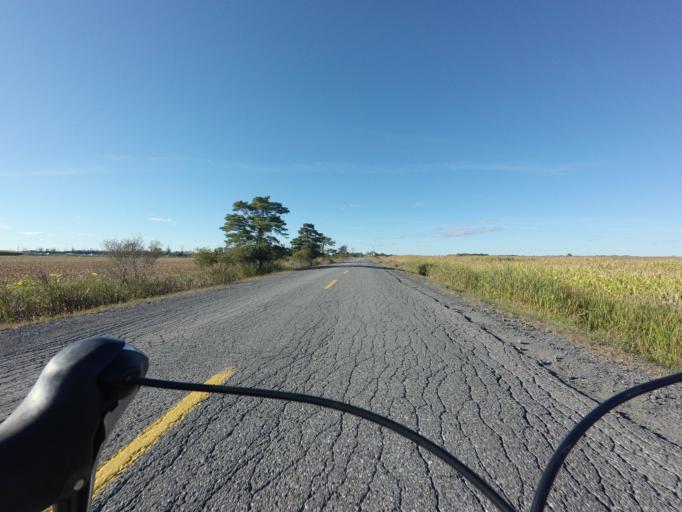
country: CA
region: Ontario
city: Bells Corners
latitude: 45.2021
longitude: -75.7914
